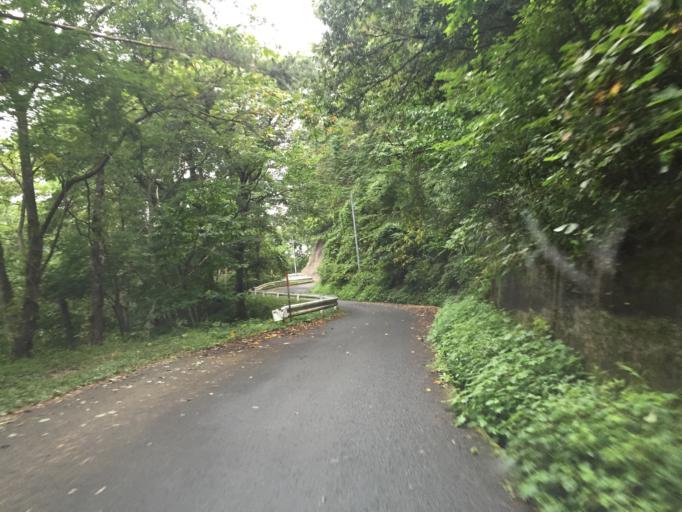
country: JP
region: Fukushima
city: Fukushima-shi
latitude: 37.8080
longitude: 140.3539
